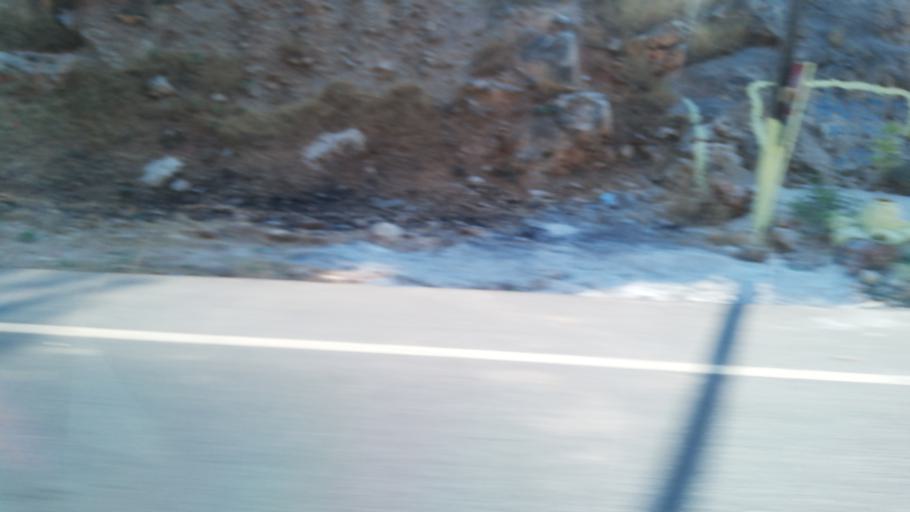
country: TR
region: Mardin
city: Sivrice
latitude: 37.2208
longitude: 41.3273
